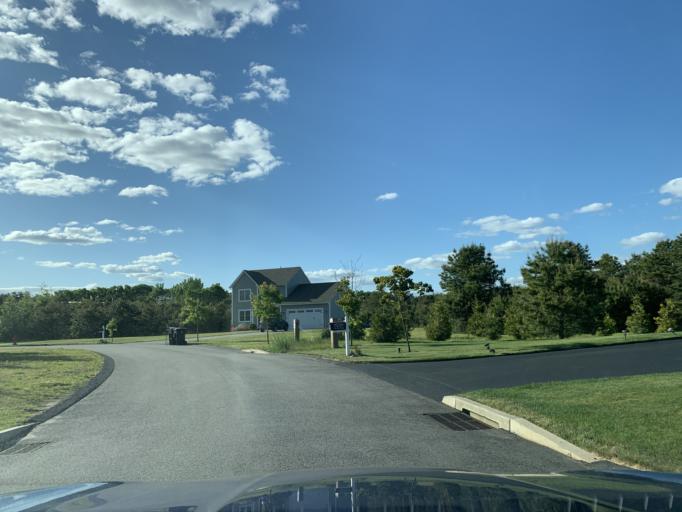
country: US
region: Rhode Island
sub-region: Kent County
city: East Greenwich
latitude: 41.6328
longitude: -71.4628
